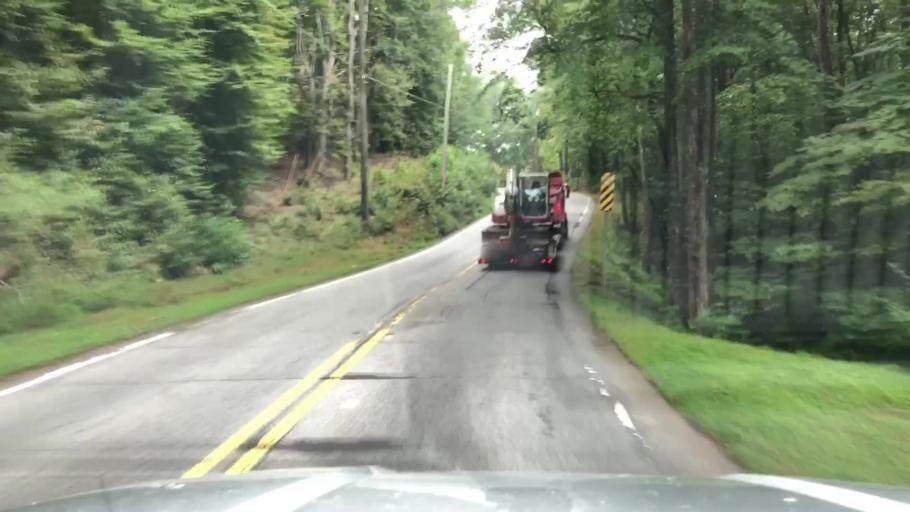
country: US
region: Georgia
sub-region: Bartow County
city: Emerson
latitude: 34.0524
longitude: -84.7821
